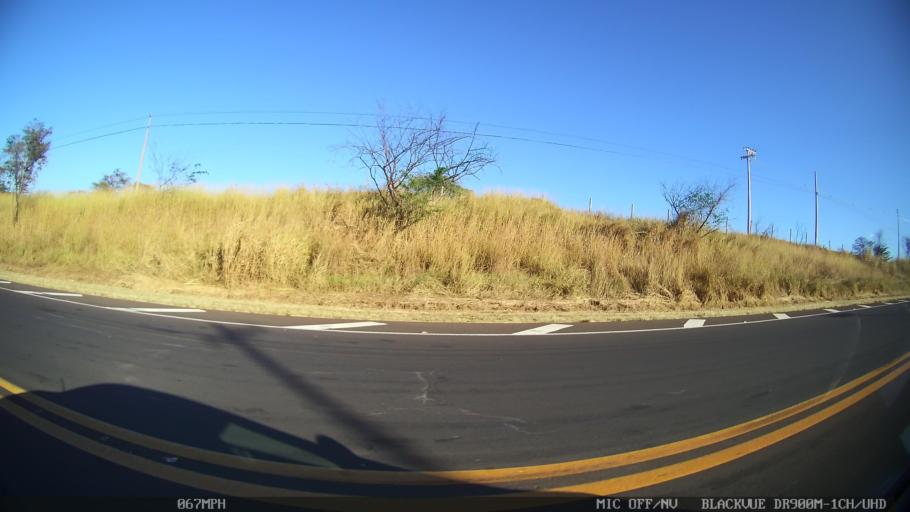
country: BR
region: Sao Paulo
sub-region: Olimpia
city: Olimpia
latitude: -20.7070
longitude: -48.9609
